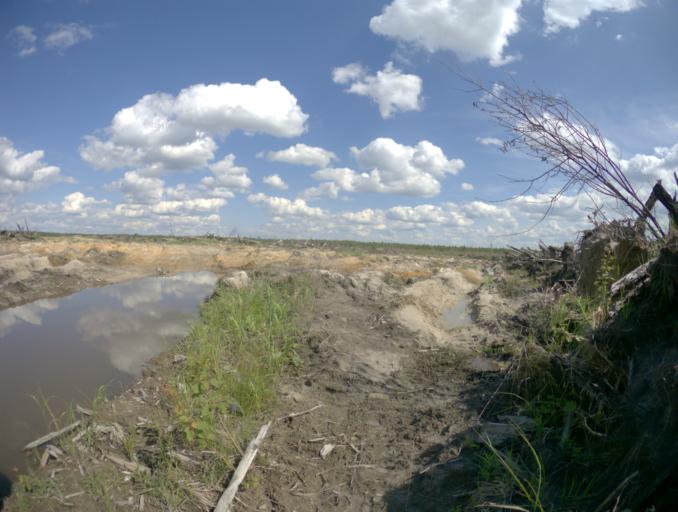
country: RU
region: Vladimir
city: Velikodvorskiy
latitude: 55.3089
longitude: 40.9099
